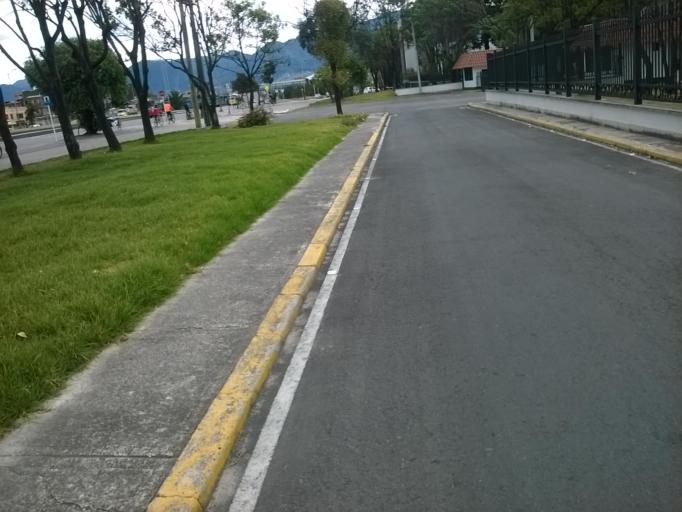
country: CO
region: Bogota D.C.
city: Bogota
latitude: 4.5934
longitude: -74.1316
